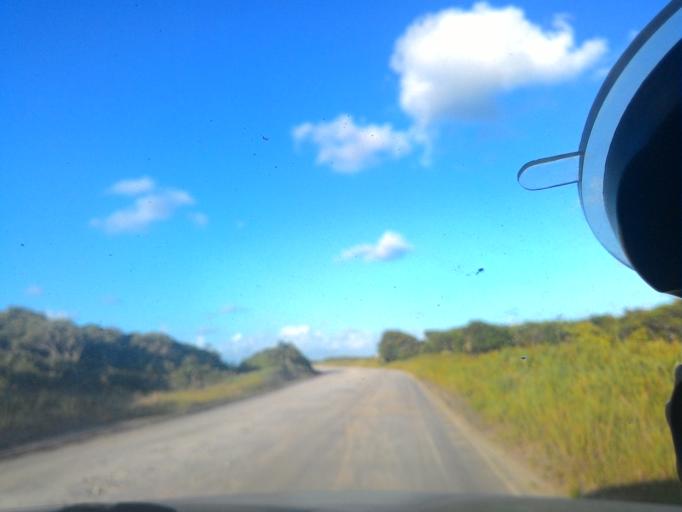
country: BR
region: Sao Paulo
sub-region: Pariquera-Acu
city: Pariquera Acu
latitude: -24.8802
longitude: -47.7364
